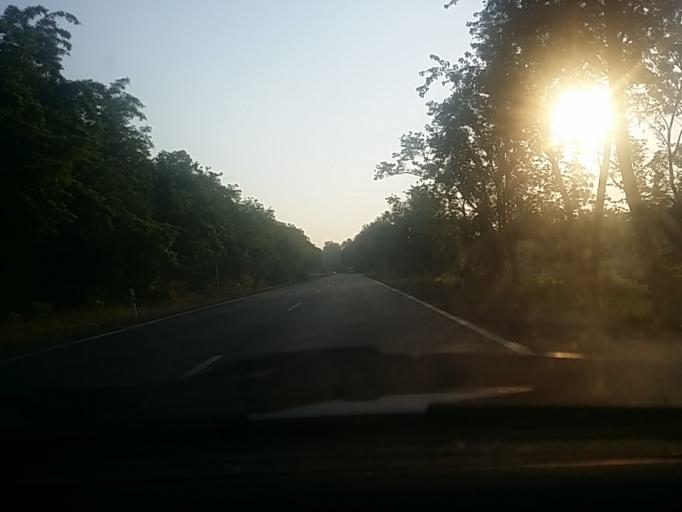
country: HU
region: Jasz-Nagykun-Szolnok
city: Jaszbereny
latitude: 47.4743
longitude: 19.8650
